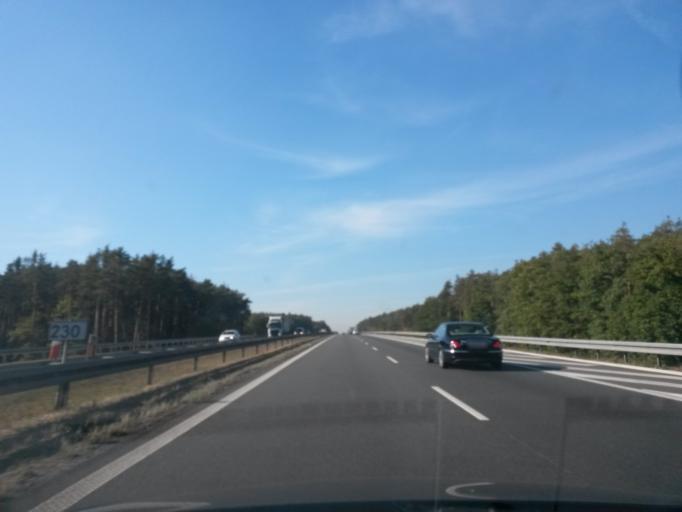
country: PL
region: Opole Voivodeship
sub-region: Powiat opolski
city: Komprachcice
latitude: 50.6155
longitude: 17.7698
